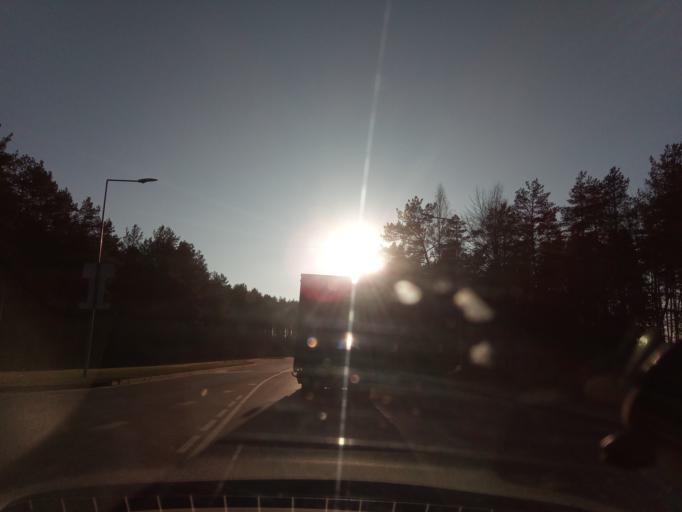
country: LT
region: Alytaus apskritis
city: Druskininkai
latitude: 54.0106
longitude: 23.9925
